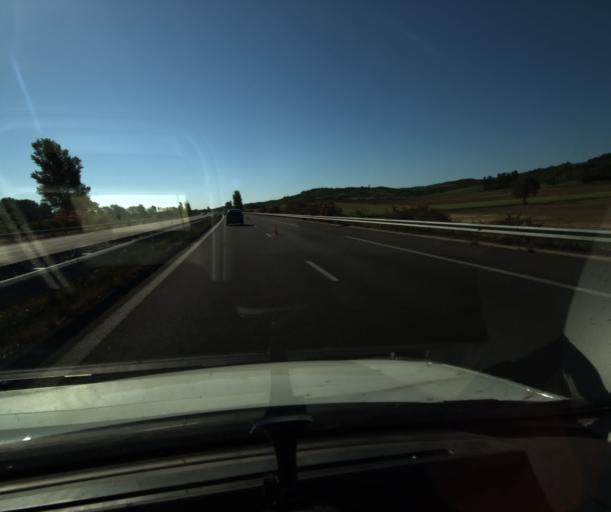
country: FR
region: Midi-Pyrenees
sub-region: Departement de la Haute-Garonne
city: Avignonet-Lauragais
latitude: 43.3268
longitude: 1.8526
